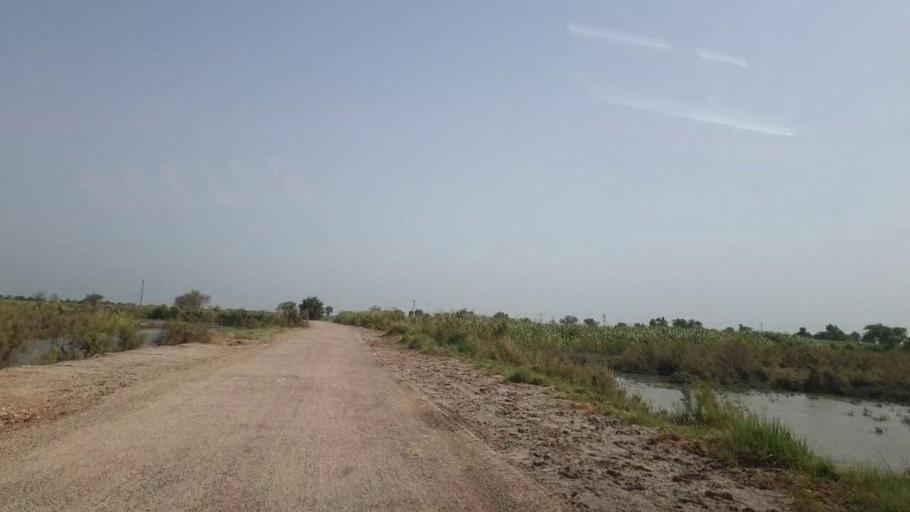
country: PK
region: Sindh
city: Sakrand
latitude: 26.3042
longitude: 68.2201
